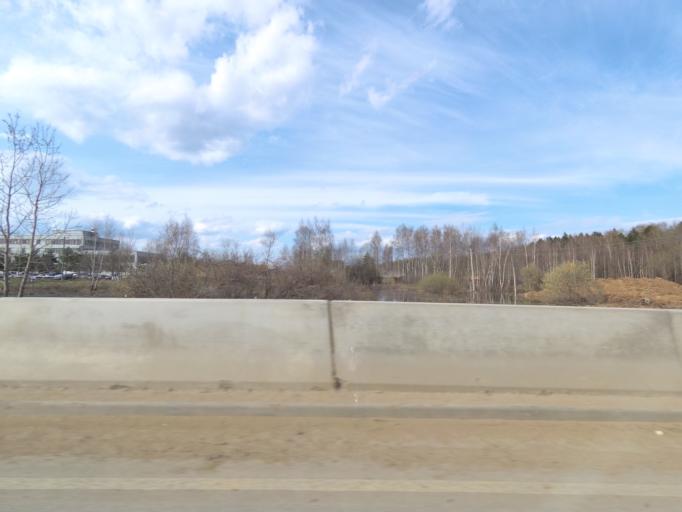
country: RU
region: Moskovskaya
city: Sheremet'yevskiy
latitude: 55.9774
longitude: 37.4545
